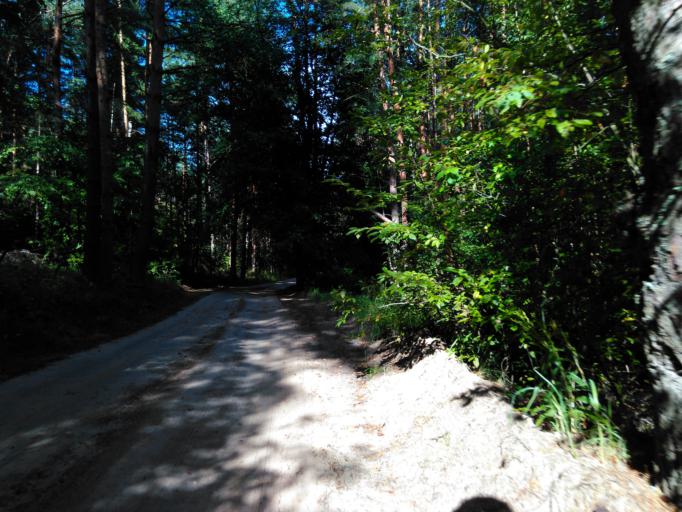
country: RU
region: Vladimir
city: Pokrov
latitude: 55.9712
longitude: 39.0850
